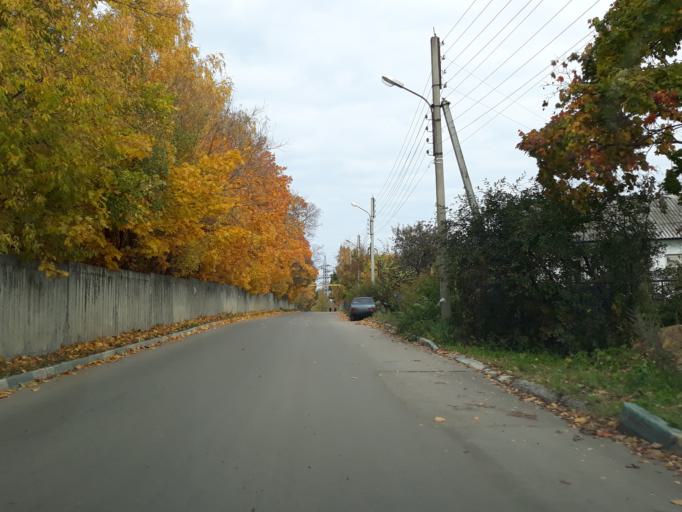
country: RU
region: Nizjnij Novgorod
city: Nizhniy Novgorod
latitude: 56.2347
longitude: 43.9779
